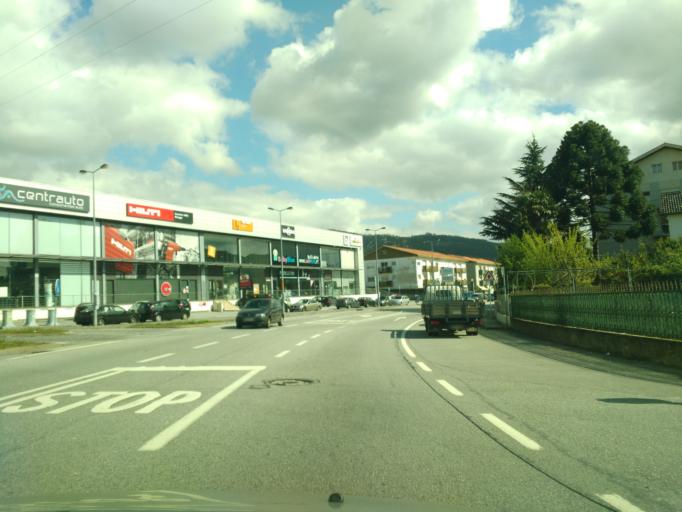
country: PT
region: Braga
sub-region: Braga
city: Braga
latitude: 41.5339
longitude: -8.4199
